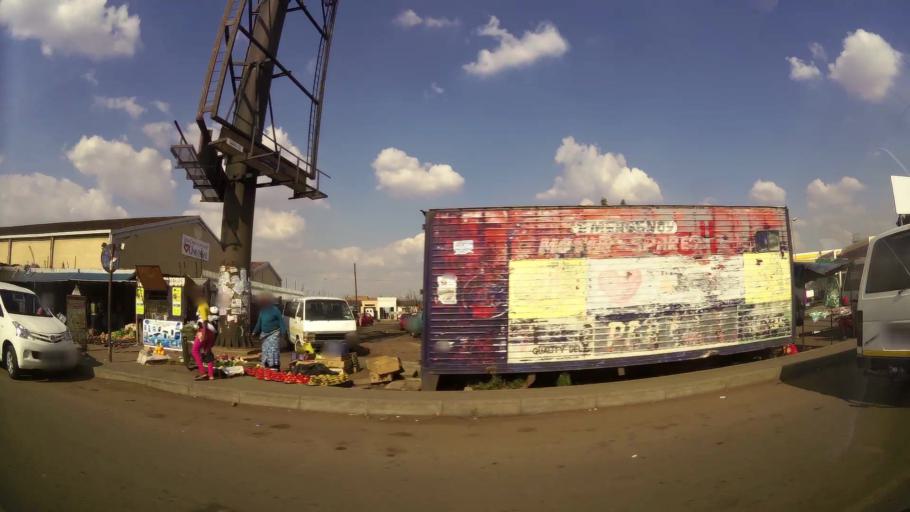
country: ZA
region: Gauteng
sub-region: Ekurhuleni Metropolitan Municipality
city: Germiston
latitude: -26.3279
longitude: 28.1437
